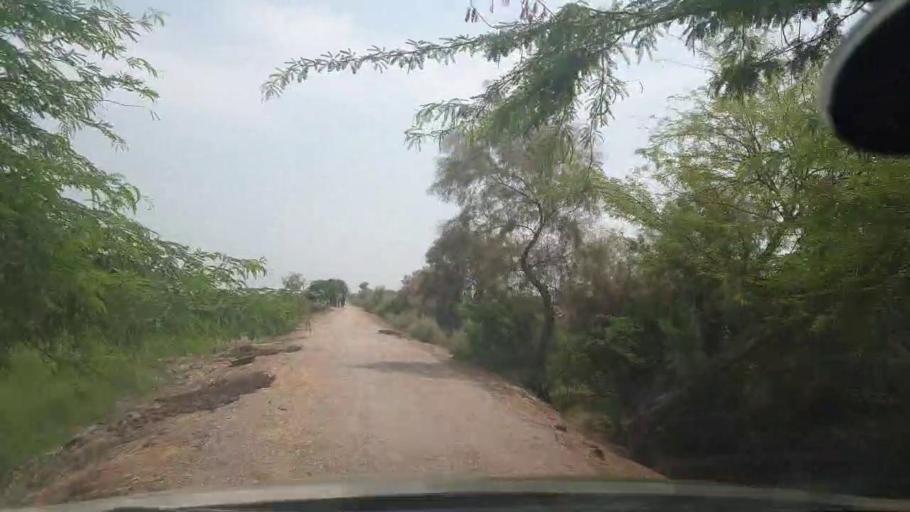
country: PK
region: Sindh
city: Jacobabad
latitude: 28.2320
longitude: 68.3880
